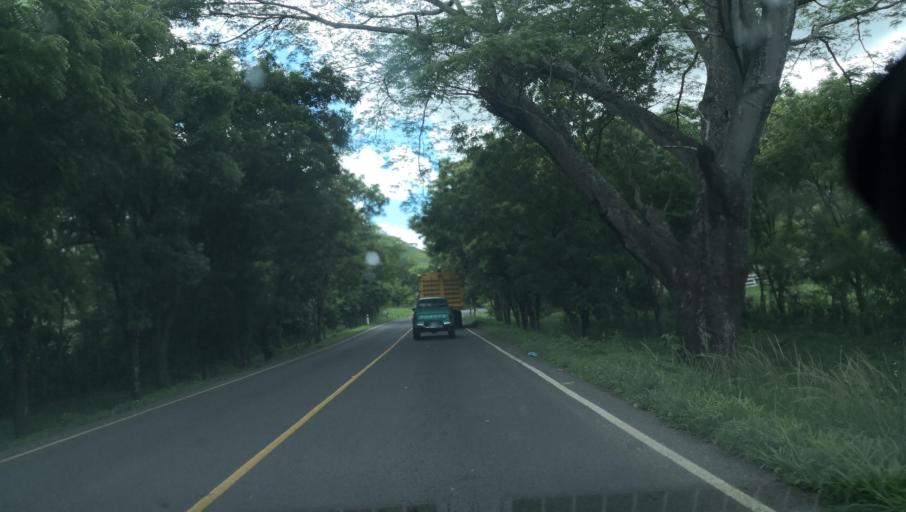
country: NI
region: Madriz
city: Yalaguina
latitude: 13.4578
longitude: -86.4583
